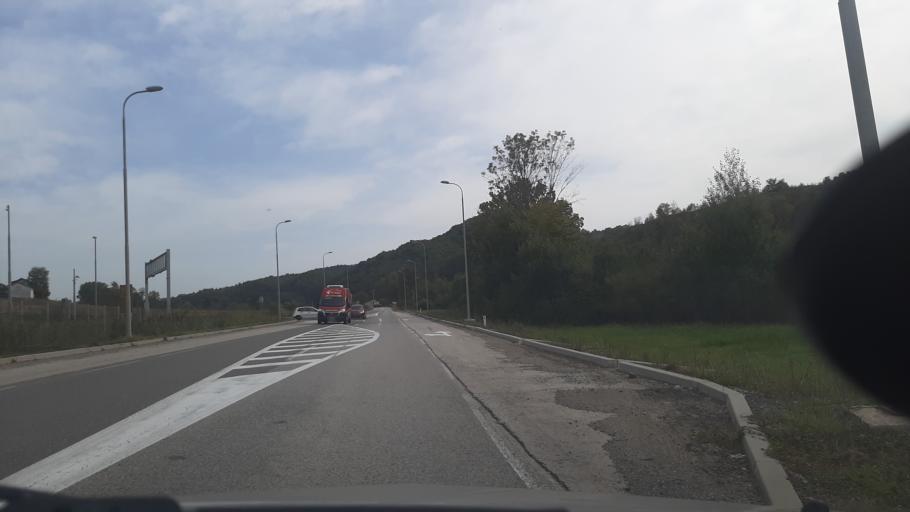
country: BA
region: Republika Srpska
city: Maglajani
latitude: 44.8699
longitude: 17.4037
